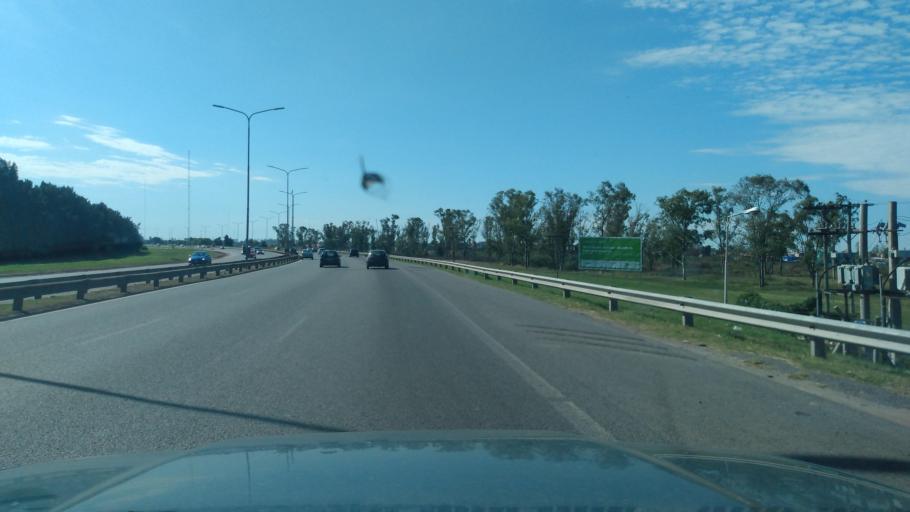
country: AR
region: Buenos Aires
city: Hurlingham
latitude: -34.5501
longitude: -58.6075
